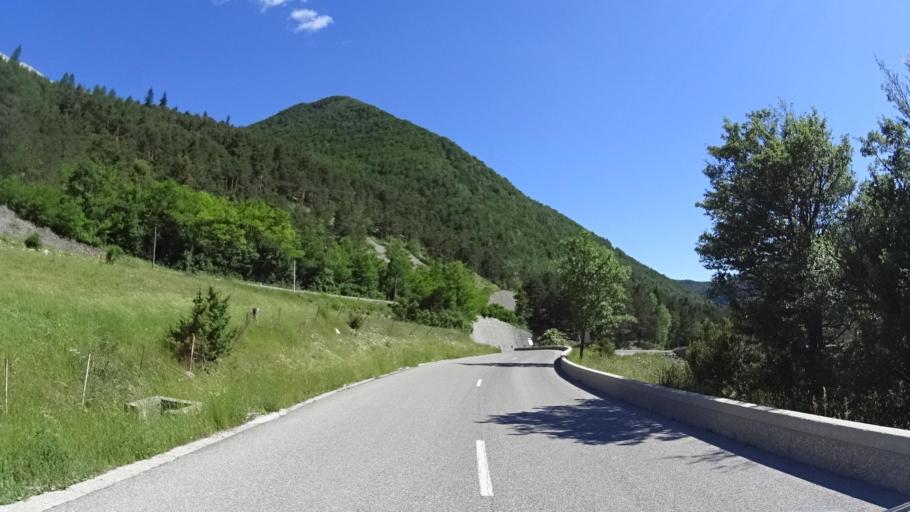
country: FR
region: Provence-Alpes-Cote d'Azur
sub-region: Departement des Alpes-de-Haute-Provence
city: Annot
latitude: 44.0386
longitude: 6.5638
